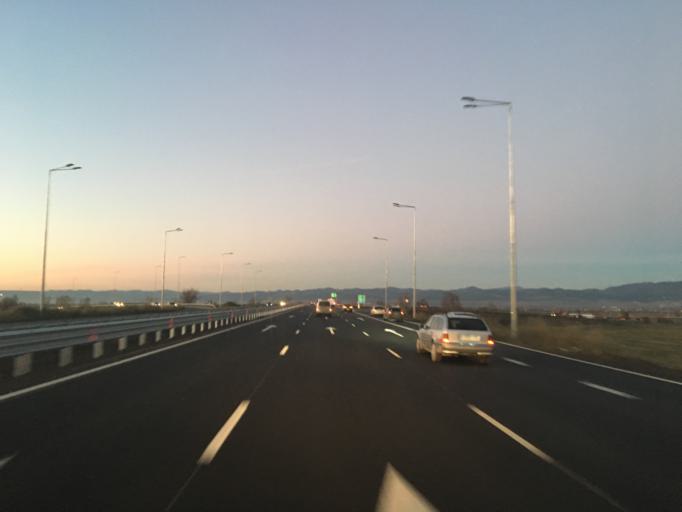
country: BG
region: Sofia-Capital
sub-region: Stolichna Obshtina
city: Sofia
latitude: 42.7038
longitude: 23.4505
